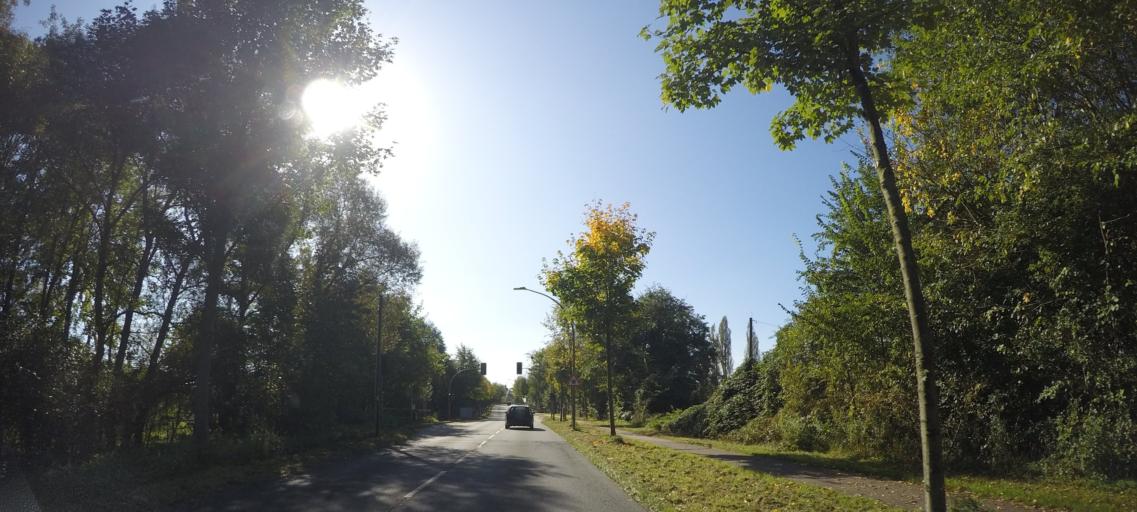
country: DE
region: North Rhine-Westphalia
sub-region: Regierungsbezirk Arnsberg
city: Hamm
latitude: 51.6968
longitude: 7.8828
